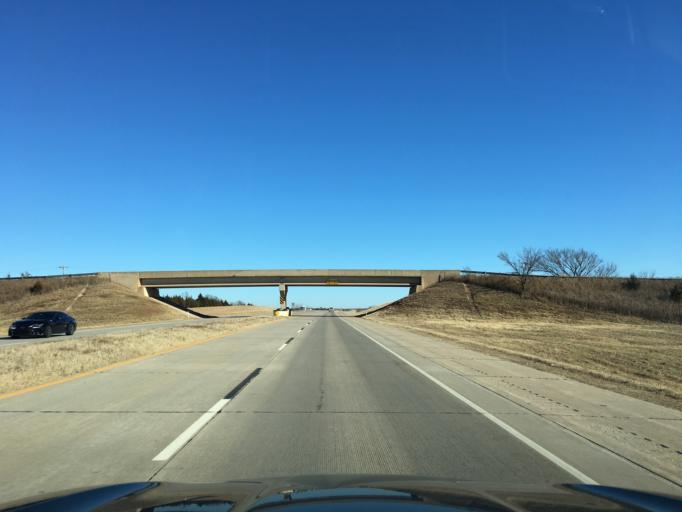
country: US
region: Oklahoma
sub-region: Payne County
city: Yale
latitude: 36.2247
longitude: -96.7142
